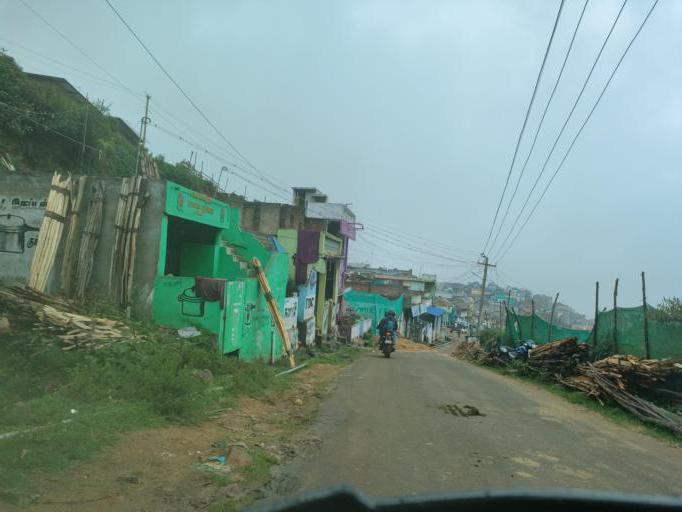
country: IN
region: Tamil Nadu
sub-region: Dindigul
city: Kodaikanal
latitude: 10.2235
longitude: 77.3443
